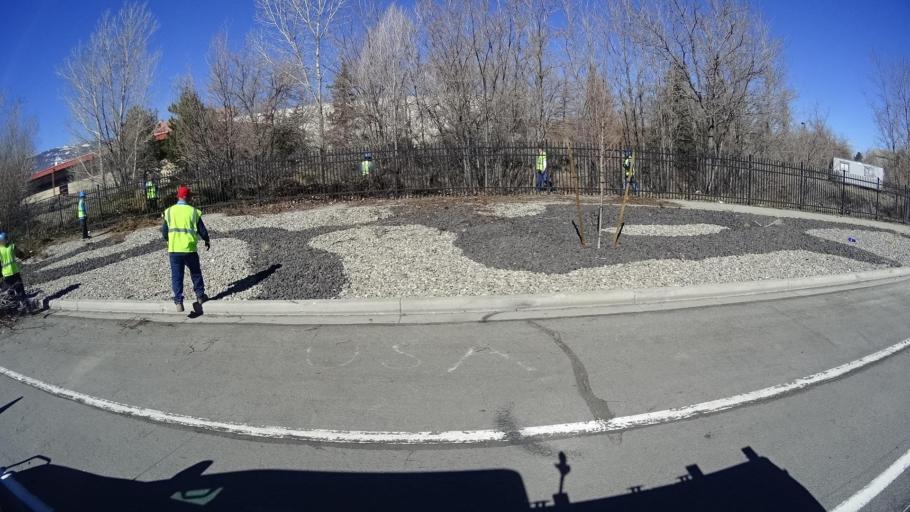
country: US
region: Nevada
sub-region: Washoe County
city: Sparks
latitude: 39.4645
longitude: -119.7718
